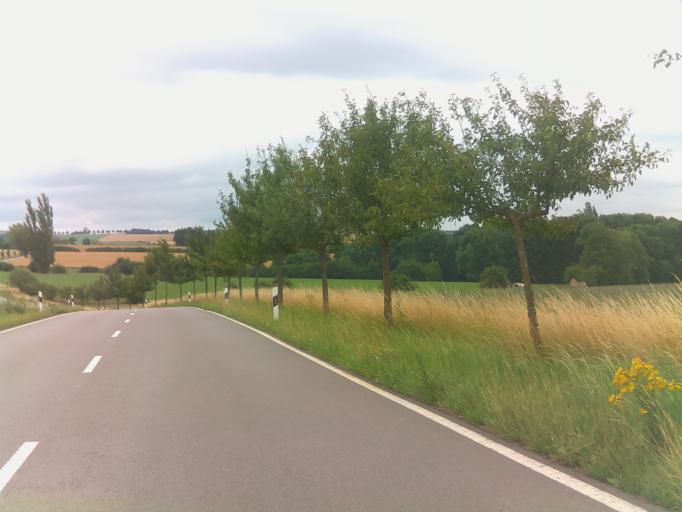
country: LU
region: Grevenmacher
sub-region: Canton de Remich
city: Mondorf-les-Bains
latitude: 49.4900
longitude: 6.3055
